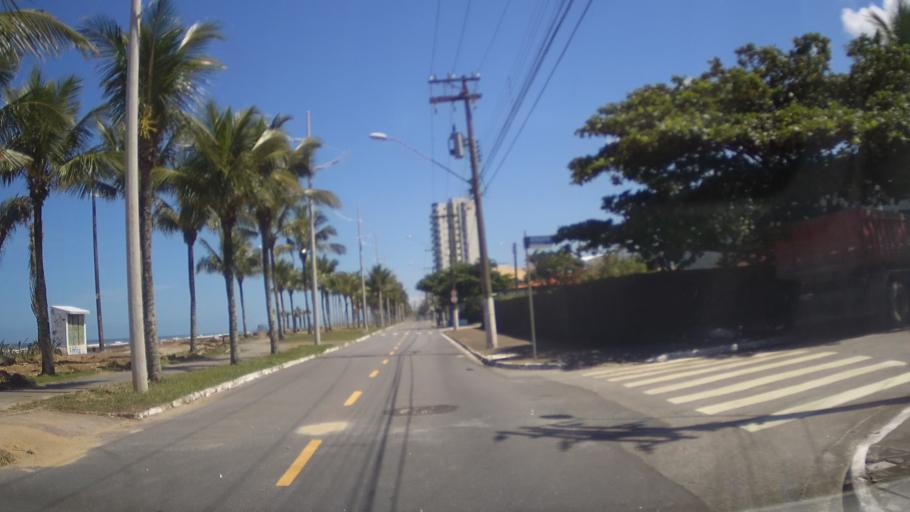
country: BR
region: Sao Paulo
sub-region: Mongagua
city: Mongagua
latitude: -24.0767
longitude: -46.5804
